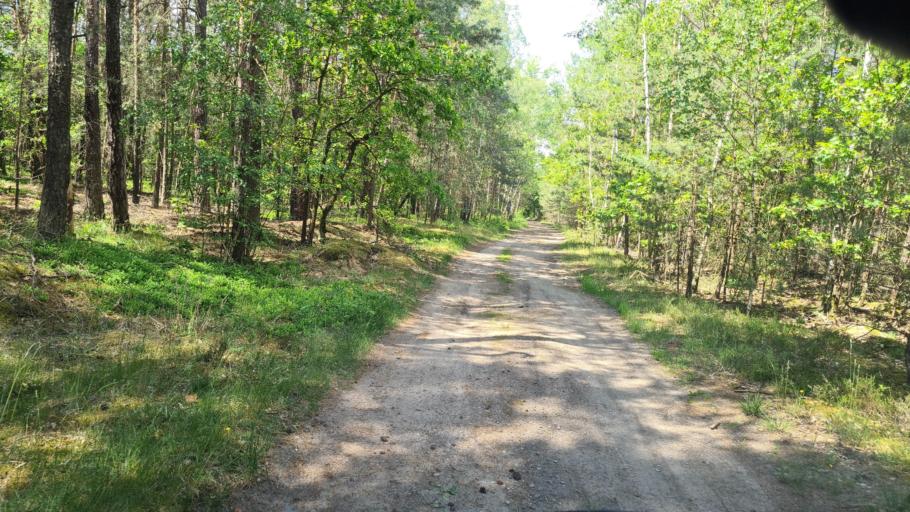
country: DE
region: Brandenburg
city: Sallgast
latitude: 51.5914
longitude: 13.8258
